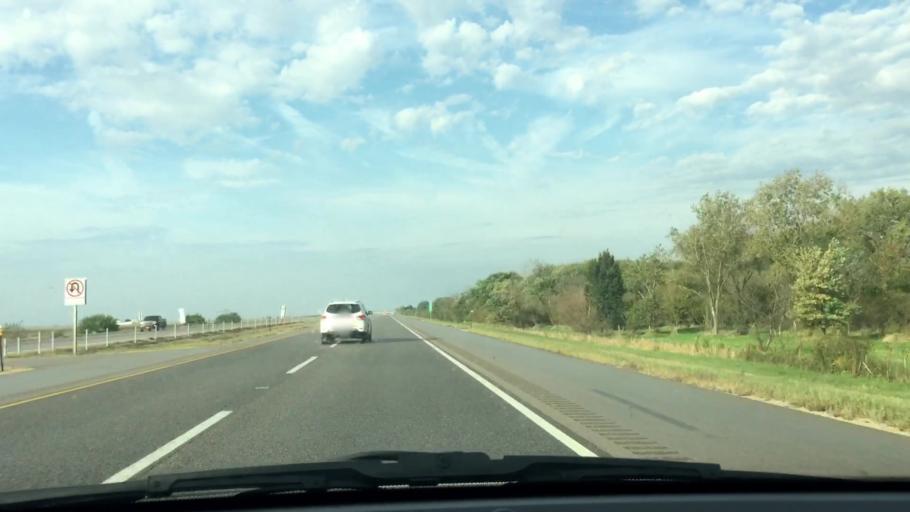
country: US
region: Illinois
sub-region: Ogle County
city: Rochelle
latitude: 41.8903
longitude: -89.0950
